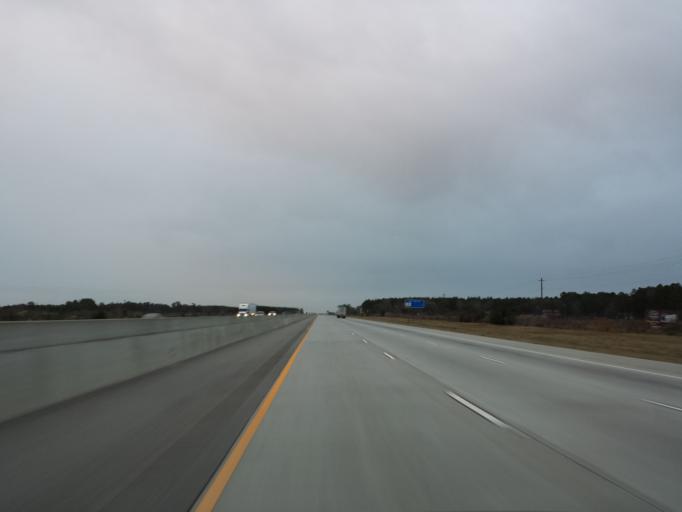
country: US
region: Georgia
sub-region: Tift County
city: Unionville
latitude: 31.3338
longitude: -83.4837
